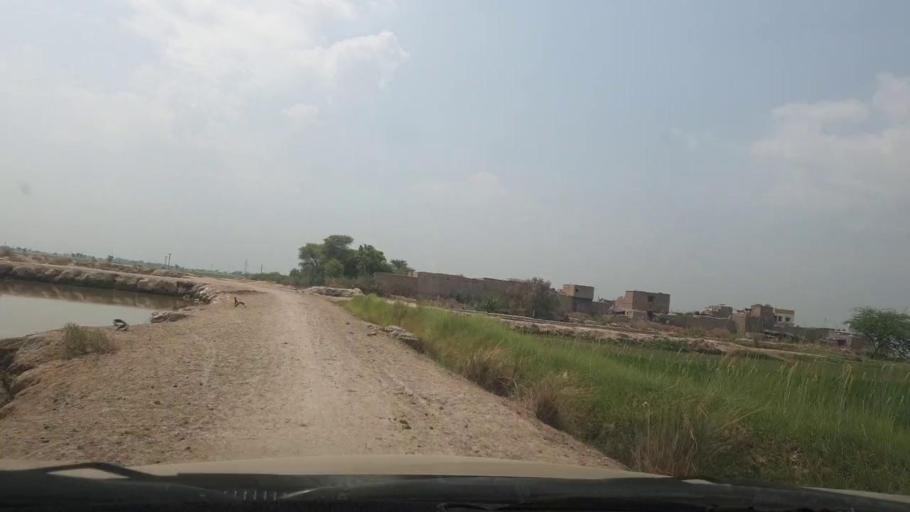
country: PK
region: Sindh
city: Naudero
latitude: 27.6929
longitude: 68.2577
